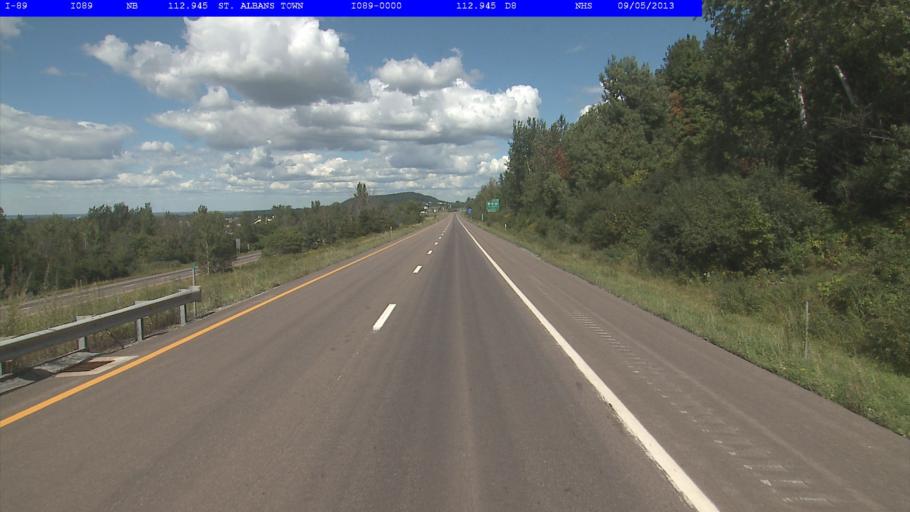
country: US
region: Vermont
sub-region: Franklin County
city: Saint Albans
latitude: 44.7834
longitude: -73.0726
